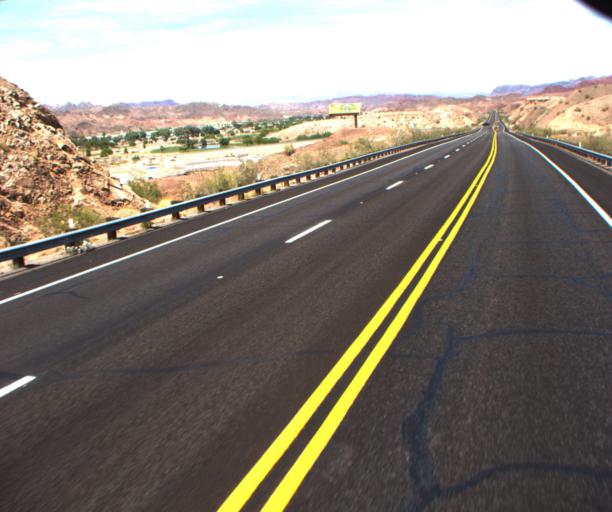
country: US
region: Arizona
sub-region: La Paz County
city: Cienega Springs
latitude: 34.2133
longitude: -114.1988
